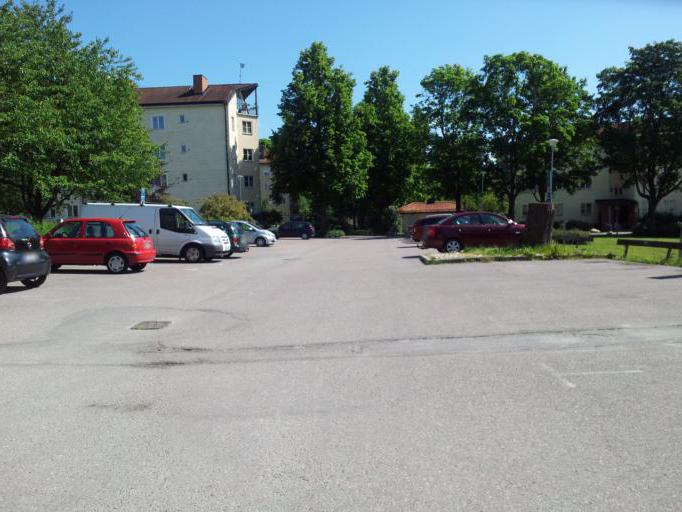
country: SE
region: Uppsala
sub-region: Uppsala Kommun
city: Uppsala
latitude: 59.8716
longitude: 17.6698
